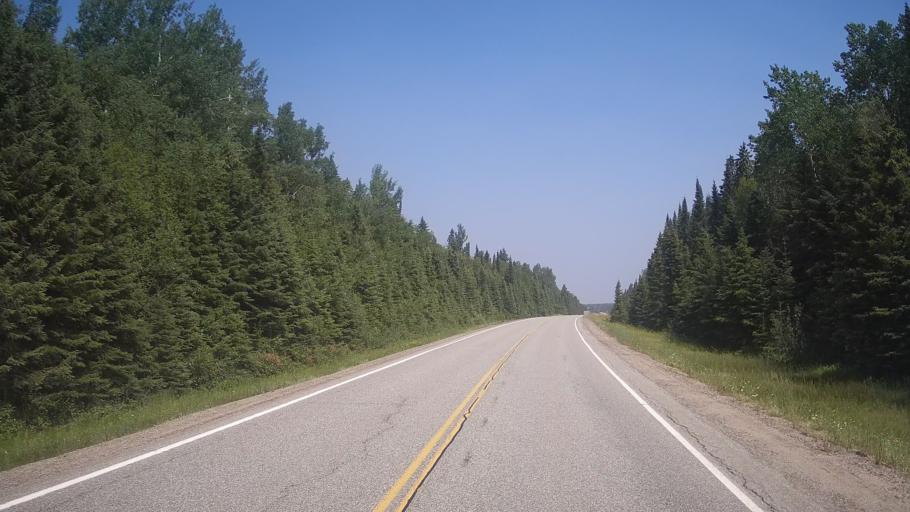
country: CA
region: Ontario
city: Timmins
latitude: 48.0840
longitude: -81.5964
